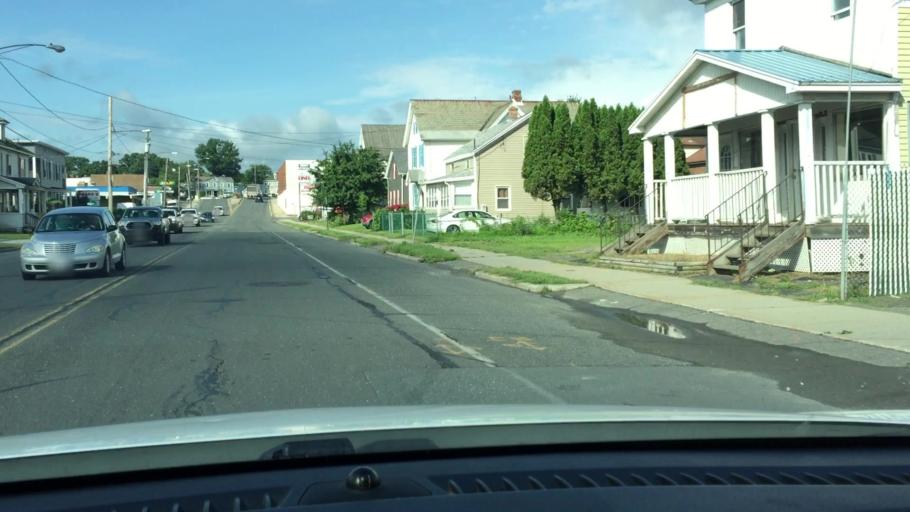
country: US
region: Massachusetts
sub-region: Berkshire County
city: Pittsfield
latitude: 42.4484
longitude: -73.2418
